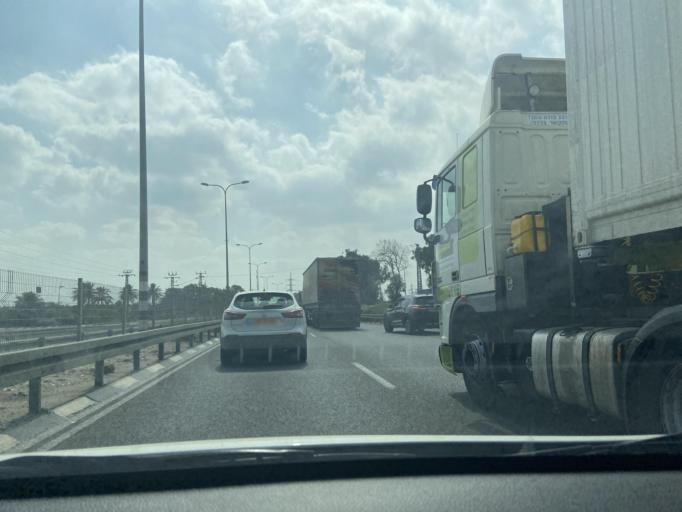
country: IL
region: Northern District
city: `Akko
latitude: 32.8998
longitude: 35.0919
